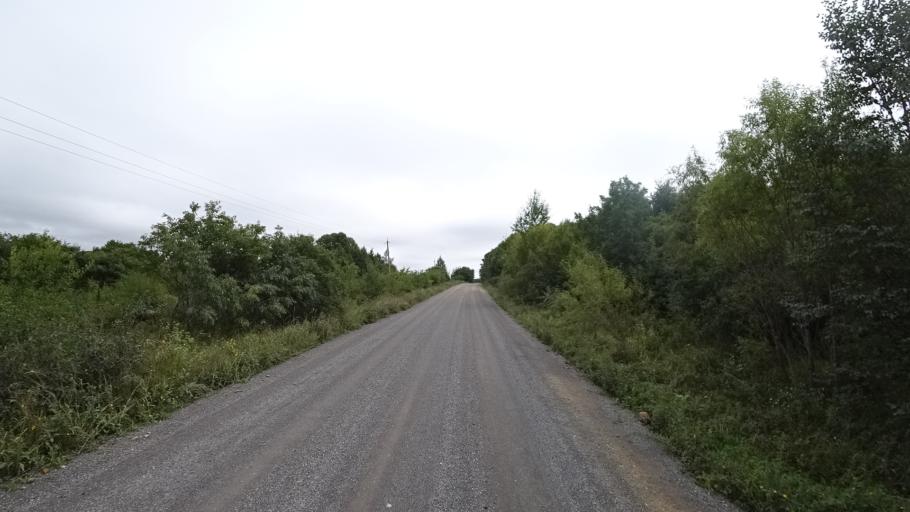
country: RU
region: Primorskiy
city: Lyalichi
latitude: 44.0716
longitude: 132.4766
